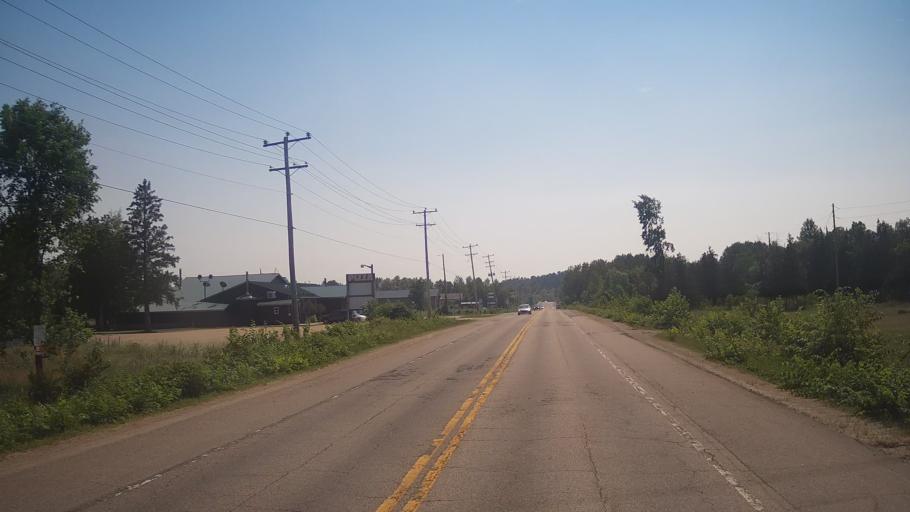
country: CA
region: Ontario
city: Pembroke
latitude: 45.8201
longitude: -77.0225
